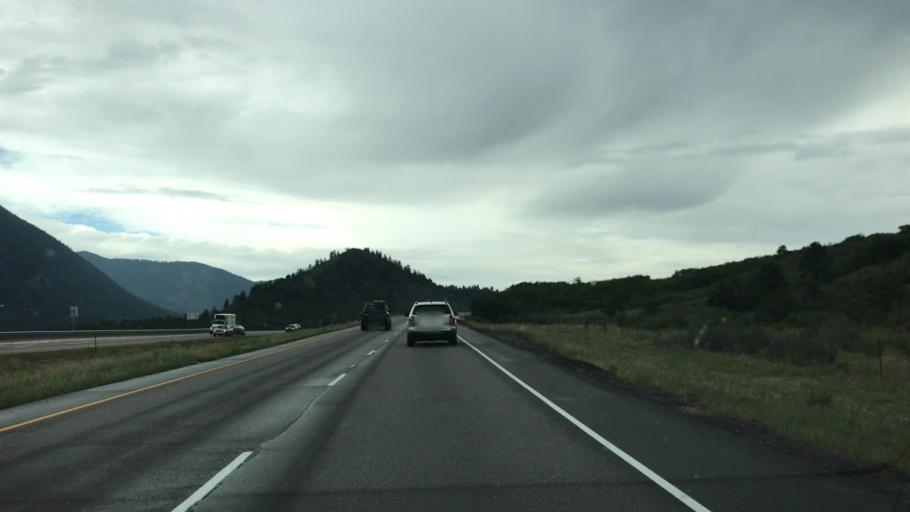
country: US
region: Colorado
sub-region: El Paso County
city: Cascade-Chipita Park
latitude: 38.9242
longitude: -104.9944
